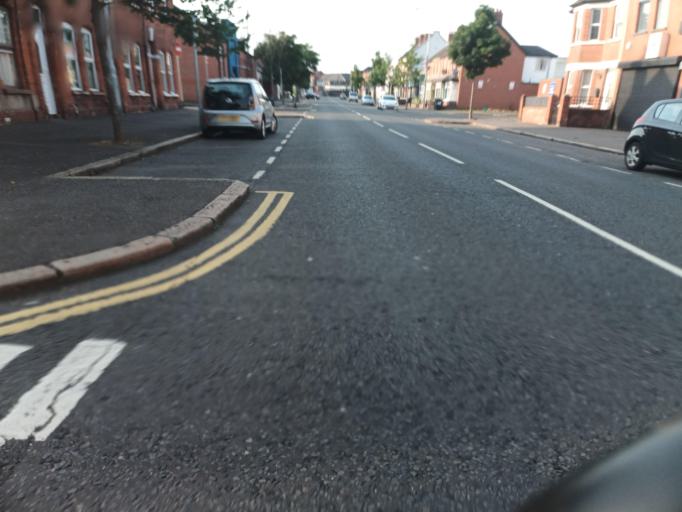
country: GB
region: Northern Ireland
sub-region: Castlereagh District
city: Castlereagh
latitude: 54.5954
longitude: -5.8881
